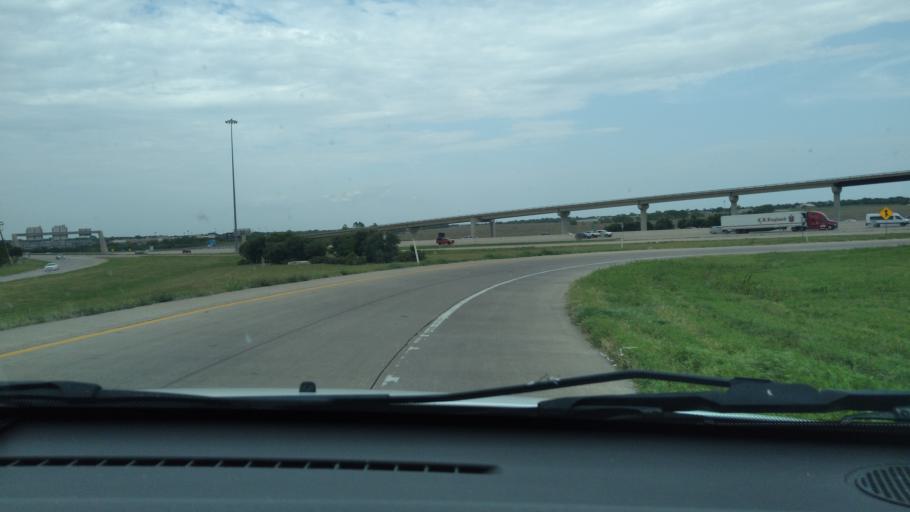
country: US
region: Texas
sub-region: McLennan County
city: Beverly Hills
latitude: 31.4956
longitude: -97.1517
